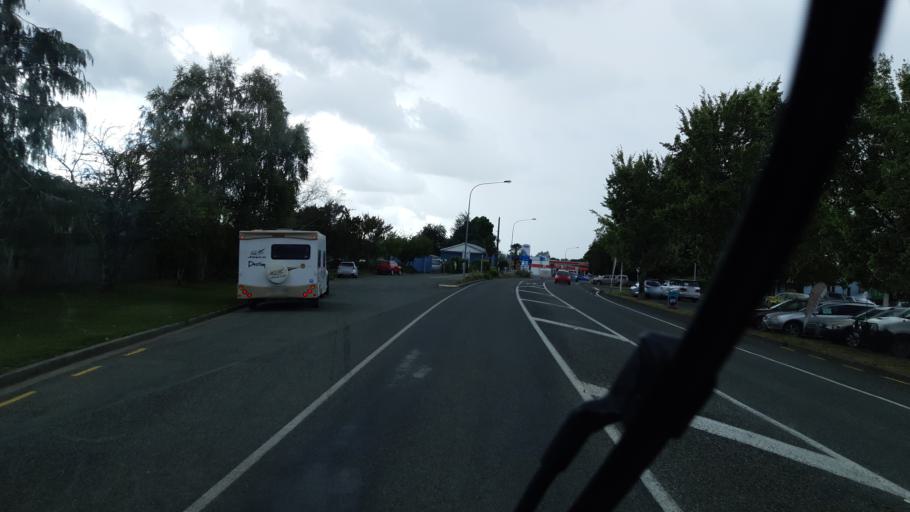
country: NZ
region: Tasman
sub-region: Tasman District
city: Wakefield
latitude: -41.4055
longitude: 173.0422
